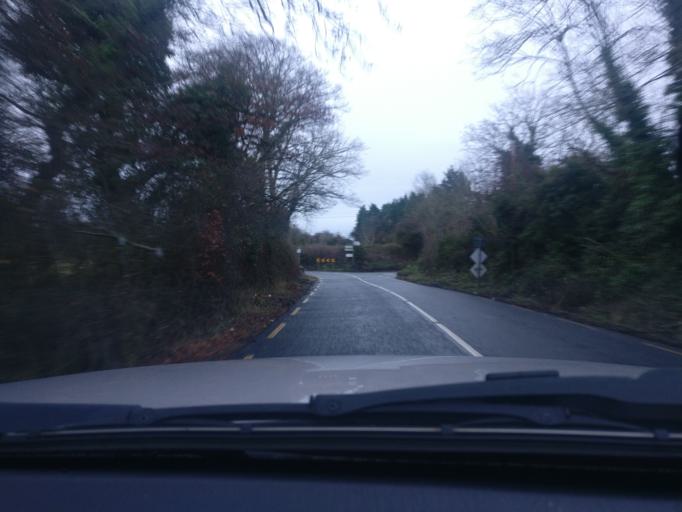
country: IE
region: Leinster
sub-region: Kildare
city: Kilcock
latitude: 53.4503
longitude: -6.6205
